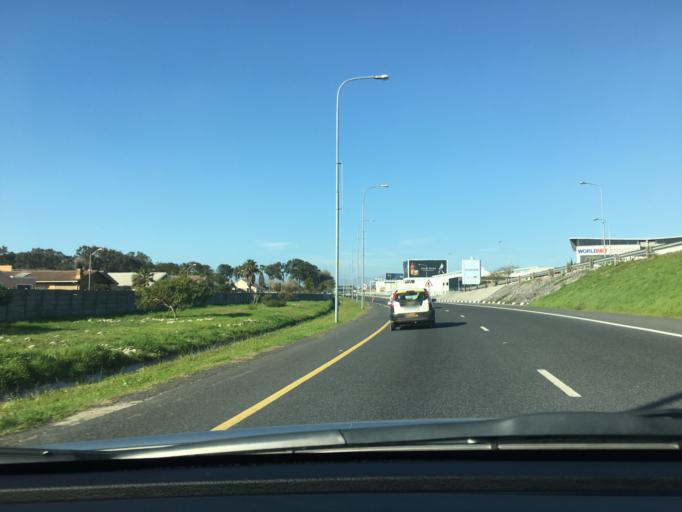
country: ZA
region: Western Cape
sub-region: City of Cape Town
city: Lansdowne
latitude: -33.9673
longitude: 18.5745
